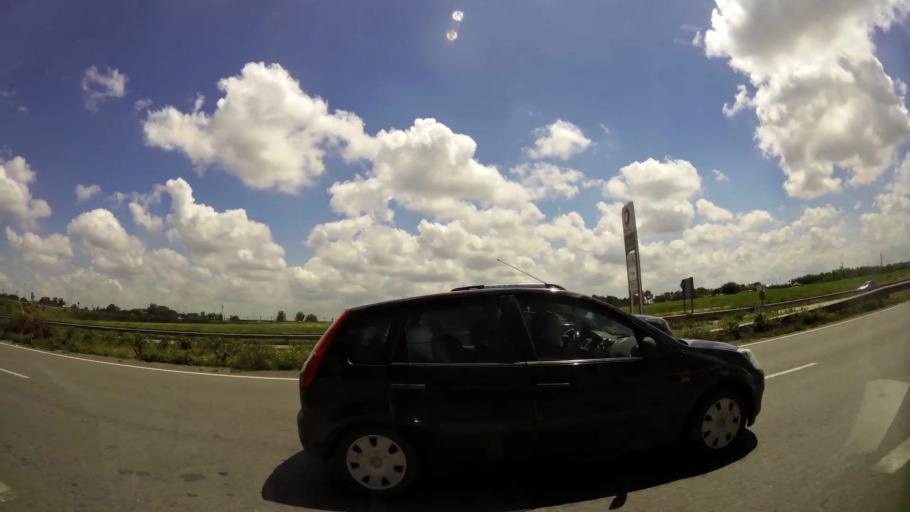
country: MA
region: Grand Casablanca
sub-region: Nouaceur
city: Bouskoura
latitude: 33.5085
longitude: -7.6141
